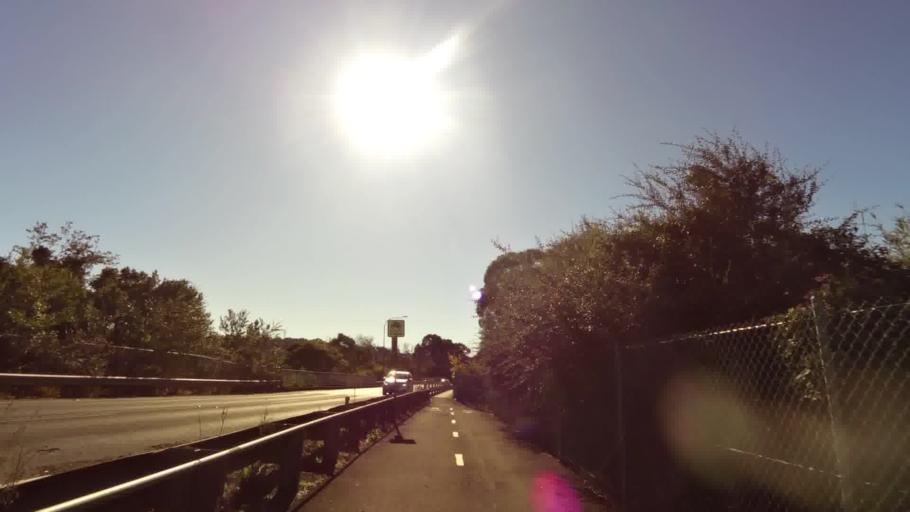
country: AU
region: New South Wales
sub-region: Wollongong
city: Koonawarra
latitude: -34.4764
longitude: 150.8088
